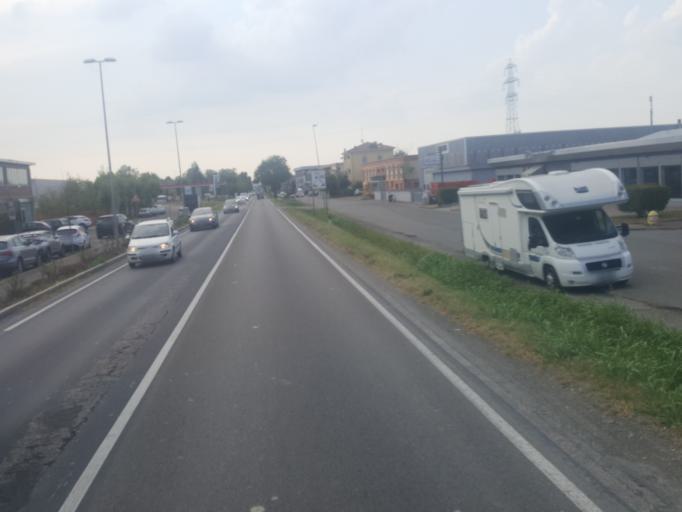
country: IT
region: Emilia-Romagna
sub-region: Provincia di Modena
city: San Damaso
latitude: 44.6255
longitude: 10.9759
